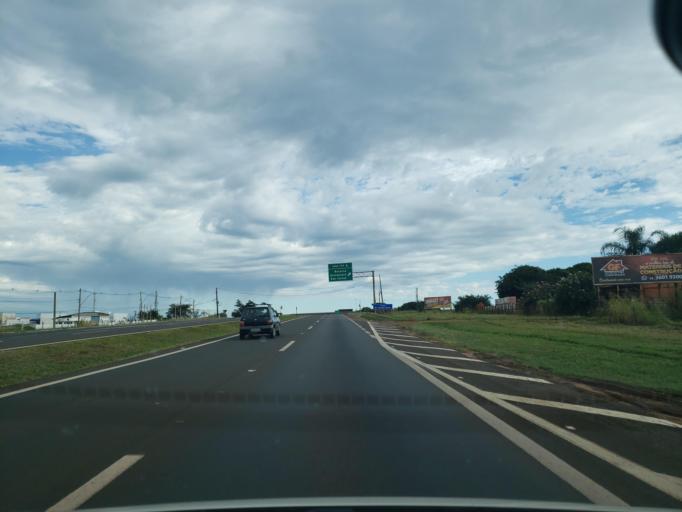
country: BR
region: Sao Paulo
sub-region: Jau
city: Jau
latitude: -22.2580
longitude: -48.5459
